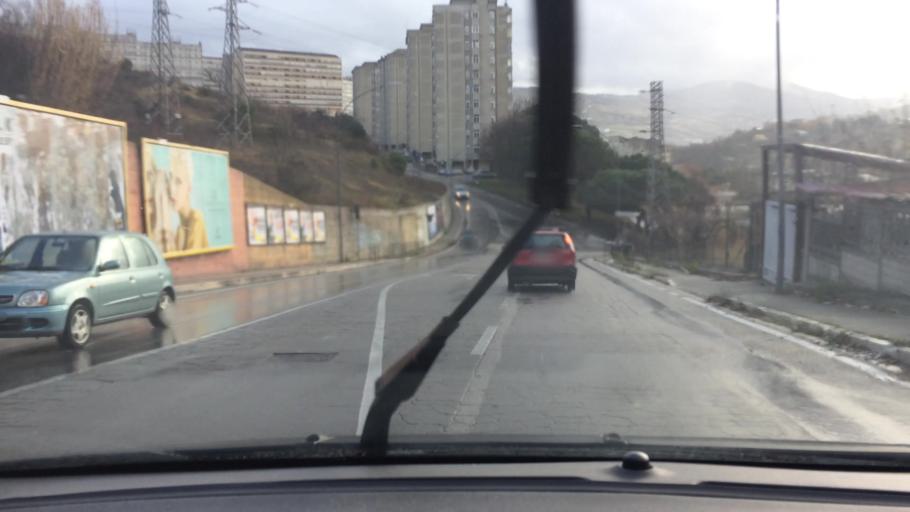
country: IT
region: Basilicate
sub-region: Provincia di Potenza
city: Potenza
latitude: 40.6366
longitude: 15.7871
